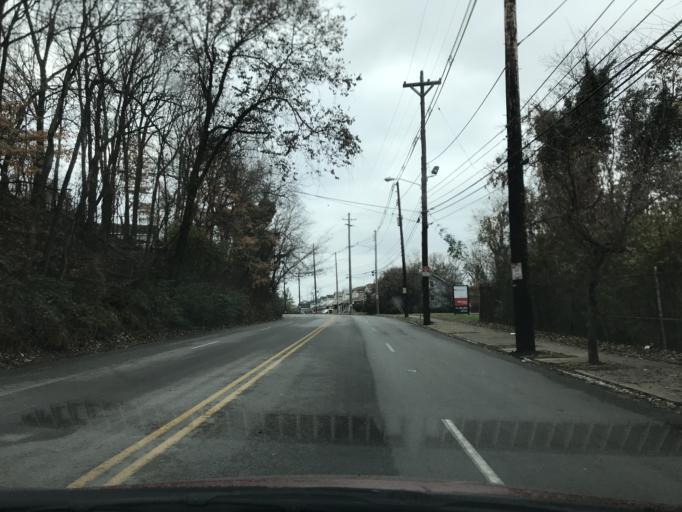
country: US
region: Indiana
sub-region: Clark County
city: Jeffersonville
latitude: 38.2510
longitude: -85.7249
